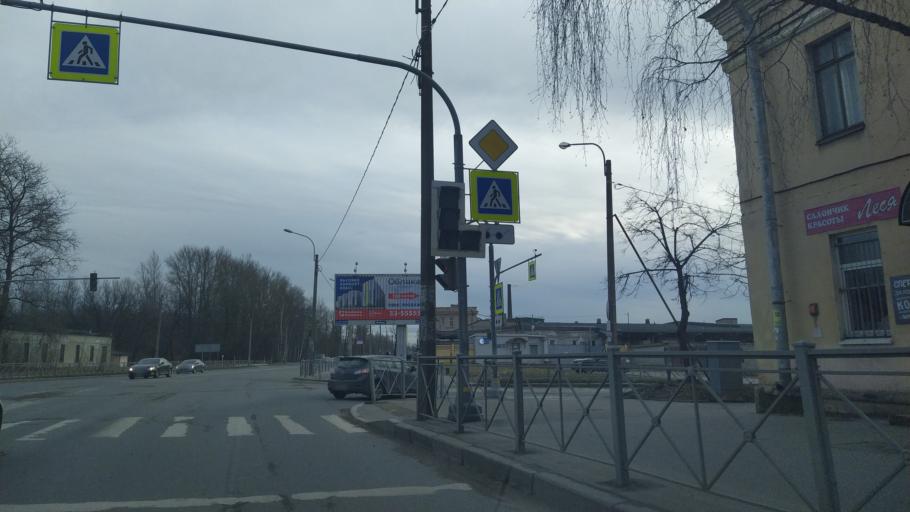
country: RU
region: St.-Petersburg
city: Kushelevka
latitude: 59.9840
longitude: 30.3620
